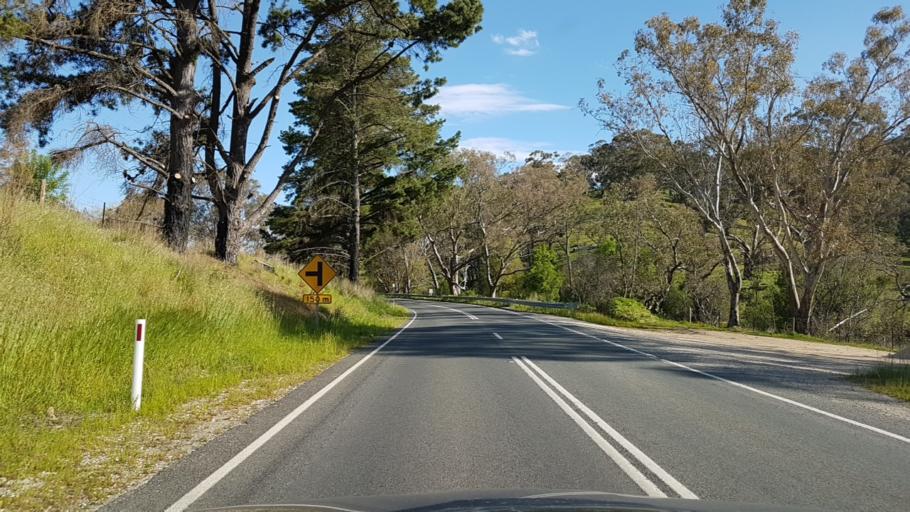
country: AU
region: South Australia
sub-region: Adelaide Hills
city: Gumeracha
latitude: -34.8314
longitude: 138.8910
